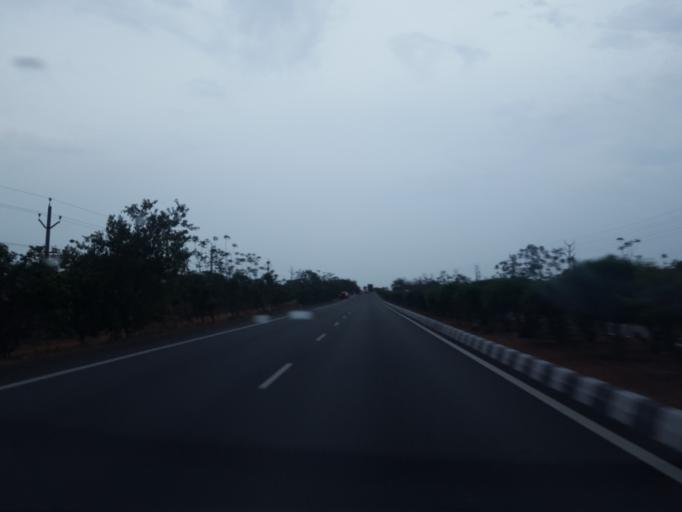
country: IN
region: Telangana
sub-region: Mahbubnagar
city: Farrukhnagar
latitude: 17.1226
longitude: 78.2739
